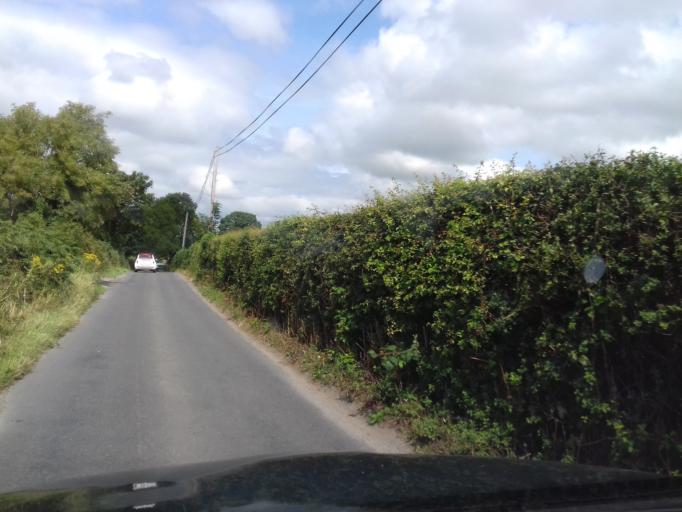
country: IE
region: Leinster
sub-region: Kilkenny
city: Graiguenamanagh
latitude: 52.5952
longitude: -6.9931
